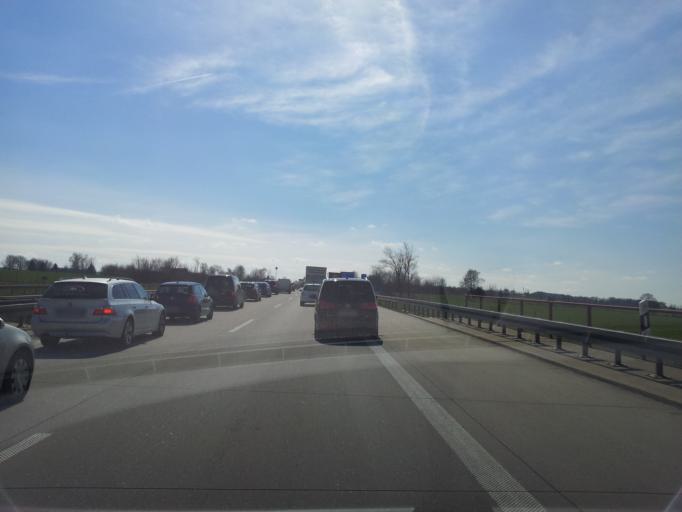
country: DE
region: Saxony
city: Niederdorf
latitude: 50.7326
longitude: 12.7798
